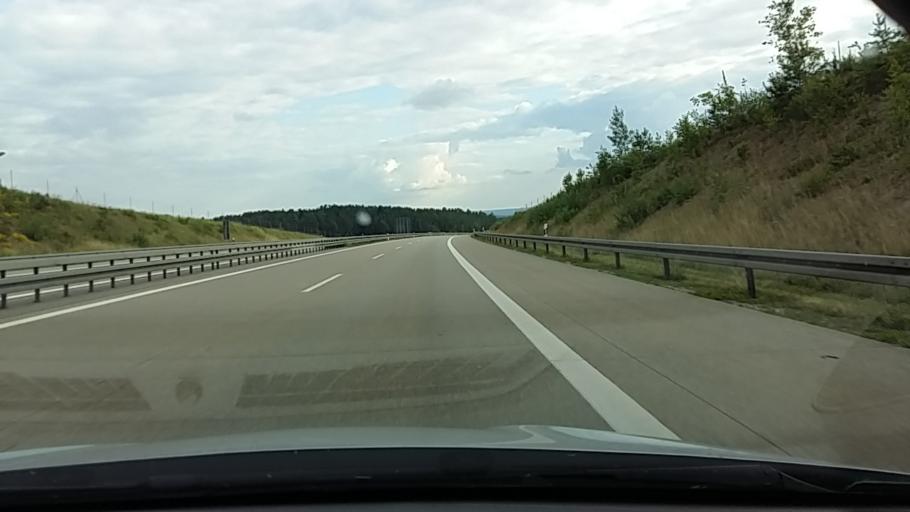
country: DE
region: Bavaria
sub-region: Upper Palatinate
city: Stulln
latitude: 49.4622
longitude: 12.1340
